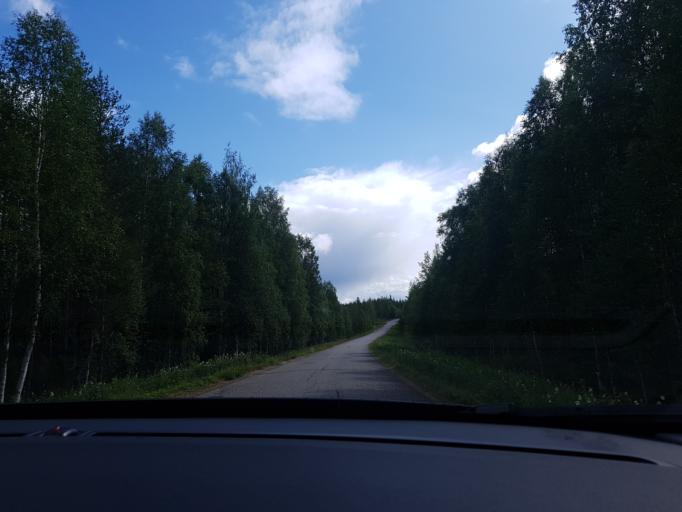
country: FI
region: Kainuu
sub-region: Kehys-Kainuu
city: Kuhmo
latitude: 64.4501
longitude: 29.6839
